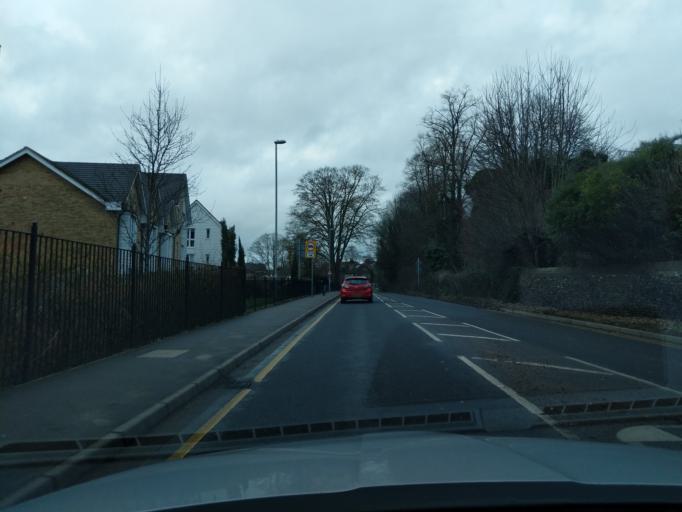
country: GB
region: England
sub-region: Hertfordshire
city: Kings Langley
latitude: 51.7286
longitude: -0.4502
